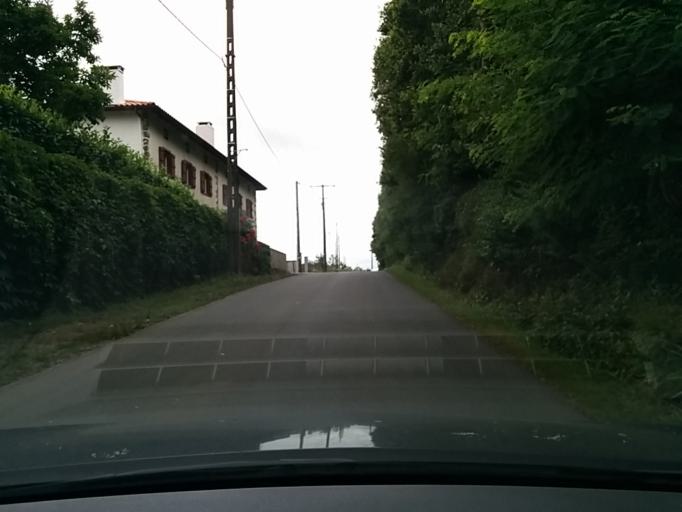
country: FR
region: Aquitaine
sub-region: Departement des Pyrenees-Atlantiques
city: Espelette
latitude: 43.3454
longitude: -1.4401
